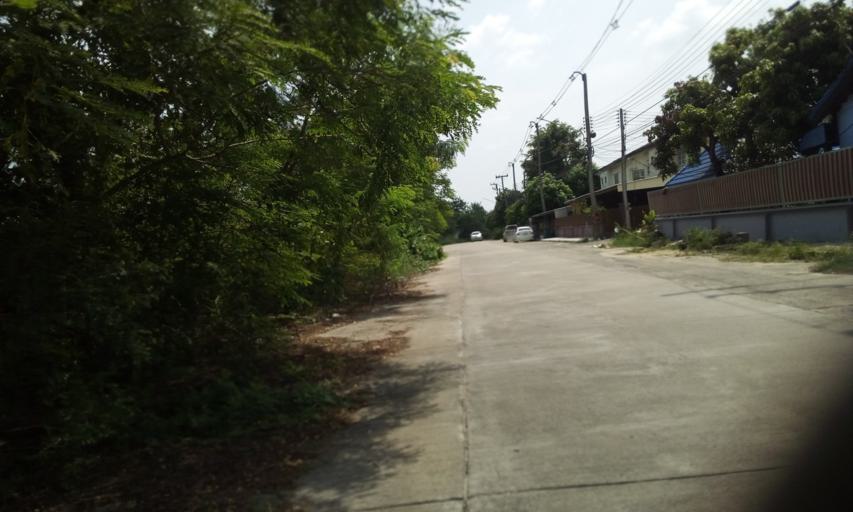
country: TH
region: Pathum Thani
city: Ban Rangsit
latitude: 14.0461
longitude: 100.8311
